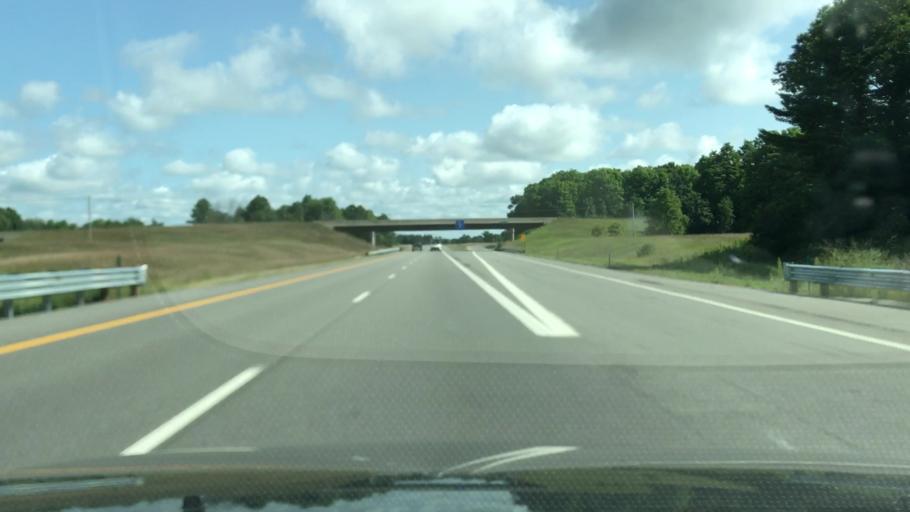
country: US
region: Michigan
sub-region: Montcalm County
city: Howard City
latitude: 43.4555
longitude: -85.4811
